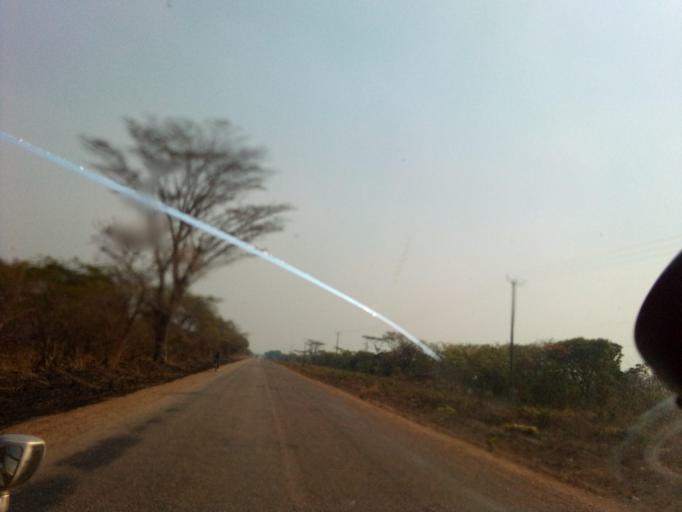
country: ZM
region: Northern
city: Chinsali
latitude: -10.9475
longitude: 32.0371
